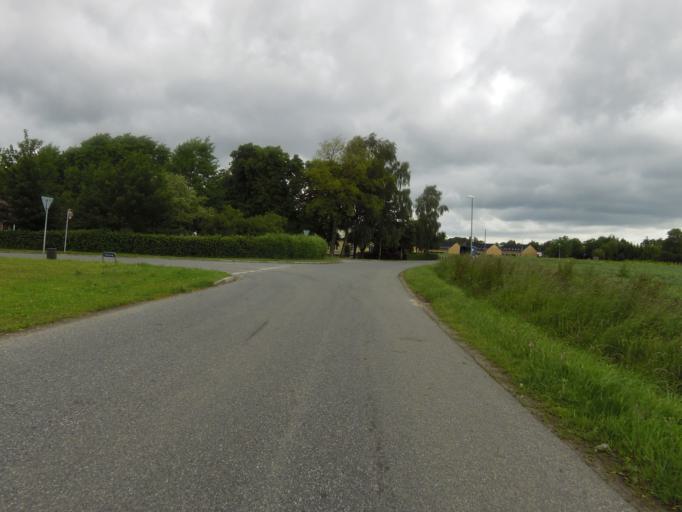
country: DK
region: South Denmark
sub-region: Haderslev Kommune
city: Gram
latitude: 55.2812
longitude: 9.0482
